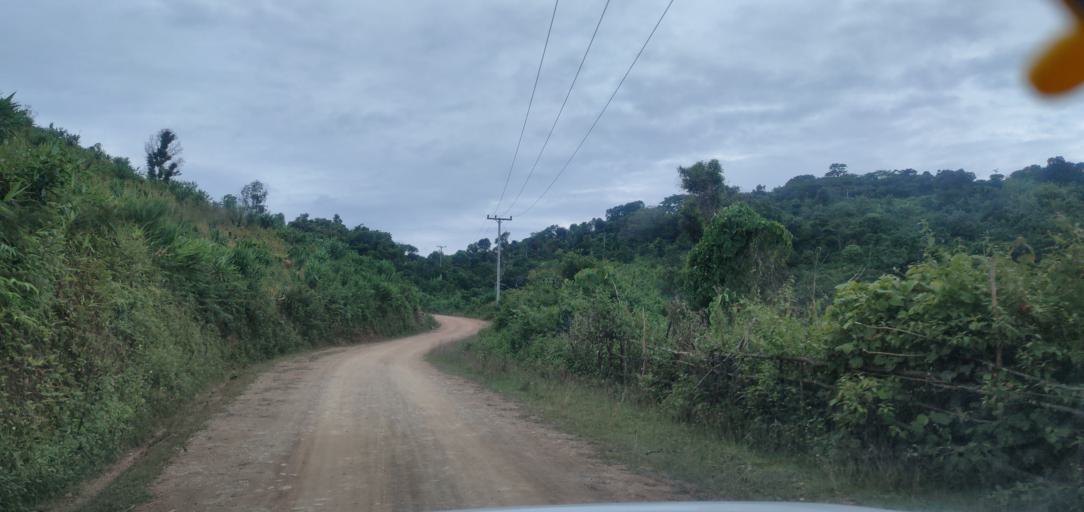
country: LA
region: Phongsali
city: Khoa
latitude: 21.1914
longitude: 102.2992
